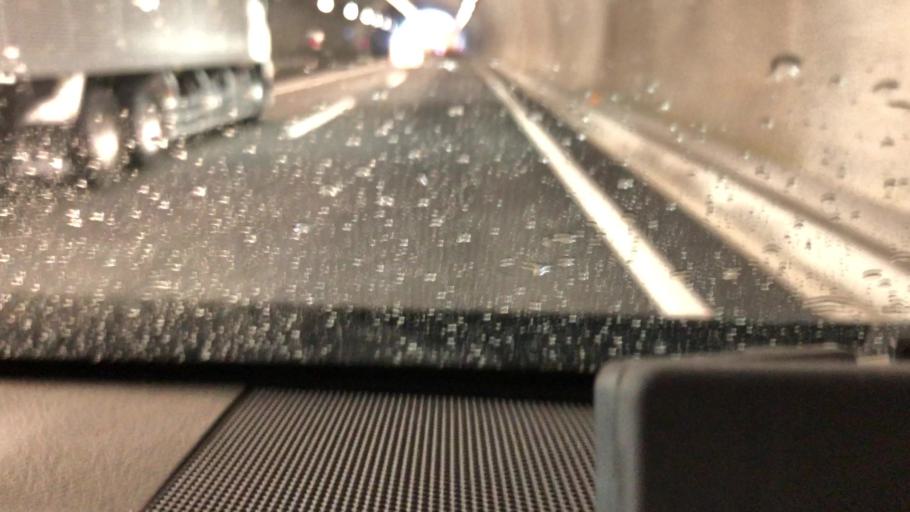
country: JP
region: Shizuoka
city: Mishima
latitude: 35.1830
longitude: 138.8875
